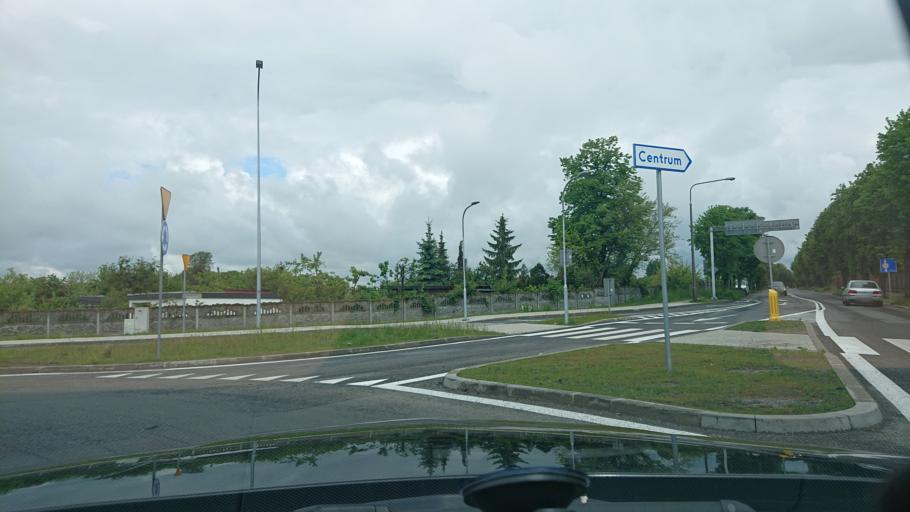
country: PL
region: Greater Poland Voivodeship
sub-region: Powiat gnieznienski
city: Gniezno
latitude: 52.5140
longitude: 17.5952
